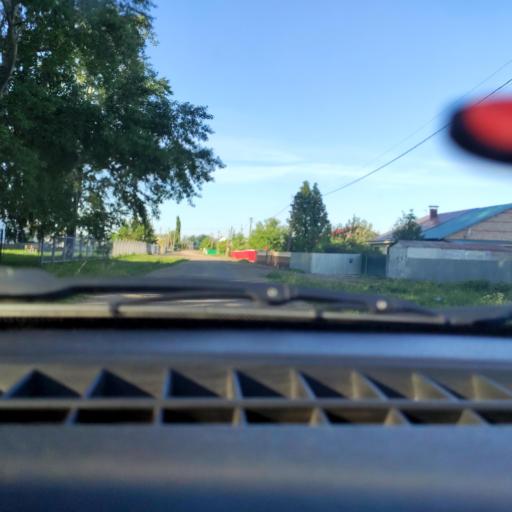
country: RU
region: Bashkortostan
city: Tolbazy
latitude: 54.2959
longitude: 55.8086
